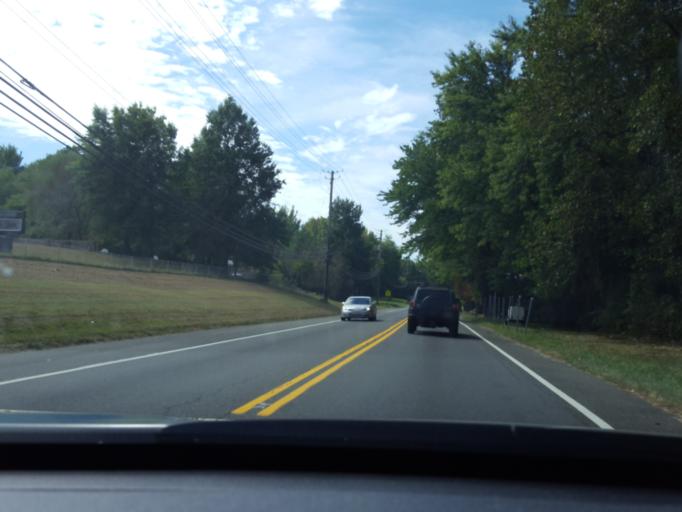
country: US
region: Maryland
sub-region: Prince George's County
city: Mellwood
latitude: 38.7917
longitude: -76.8386
